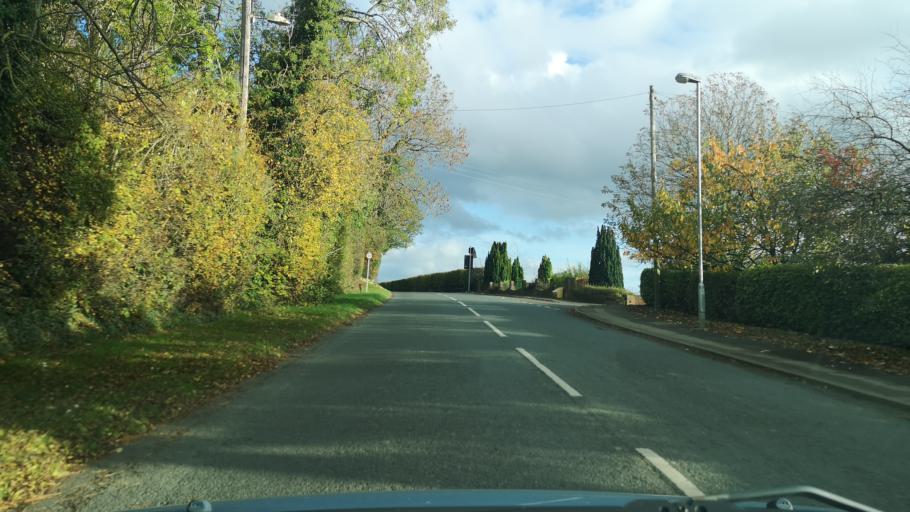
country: GB
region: England
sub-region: City and Borough of Wakefield
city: Notton
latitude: 53.6129
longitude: -1.4672
